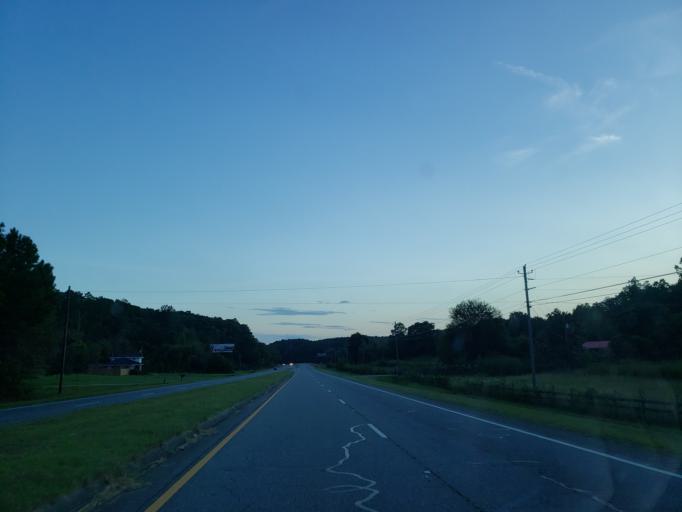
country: US
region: Georgia
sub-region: Polk County
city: Cedartown
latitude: 34.1129
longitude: -85.2283
